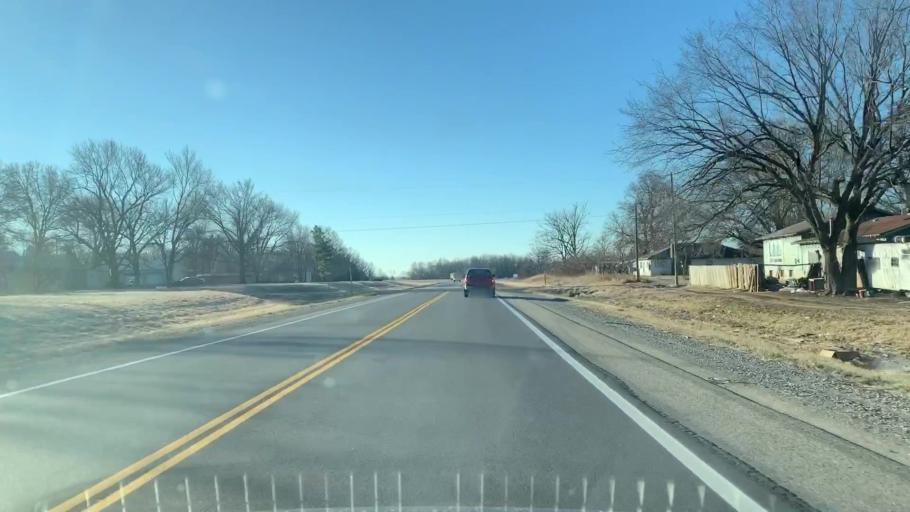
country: US
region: Kansas
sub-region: Crawford County
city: Arma
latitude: 37.5267
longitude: -94.7112
